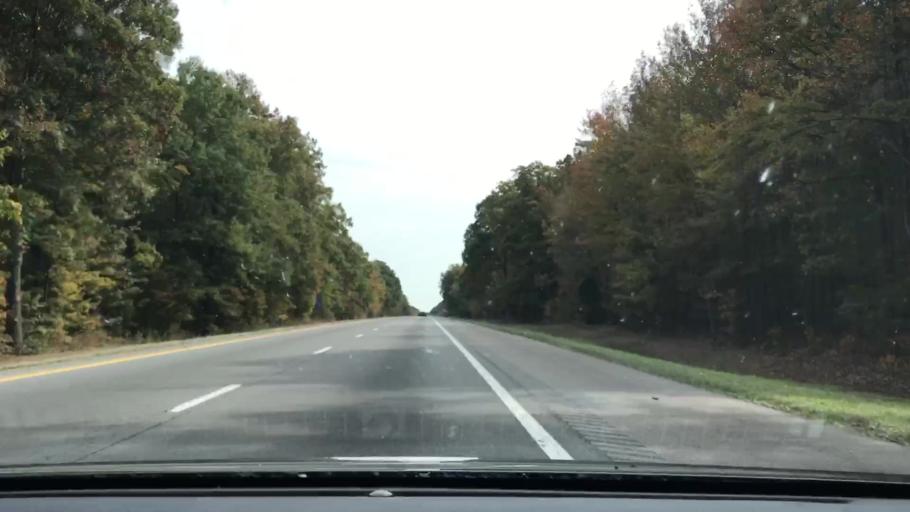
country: US
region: Tennessee
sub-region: Cheatham County
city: Pleasant View
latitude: 36.4193
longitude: -87.0534
